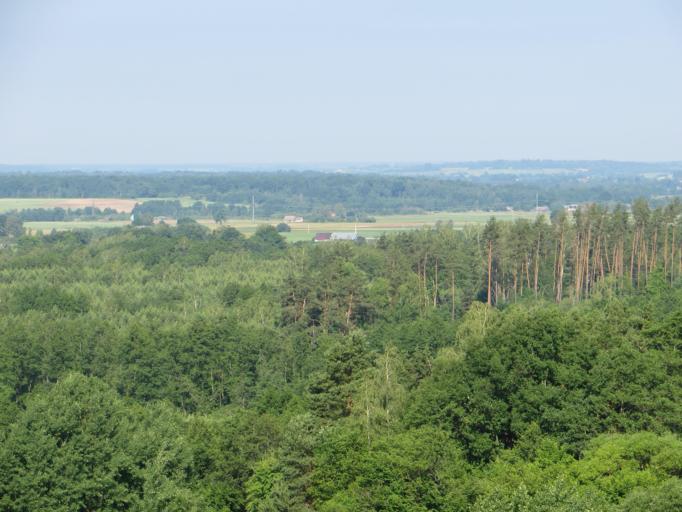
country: LT
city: Aukstadvaris
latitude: 54.5598
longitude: 24.3928
